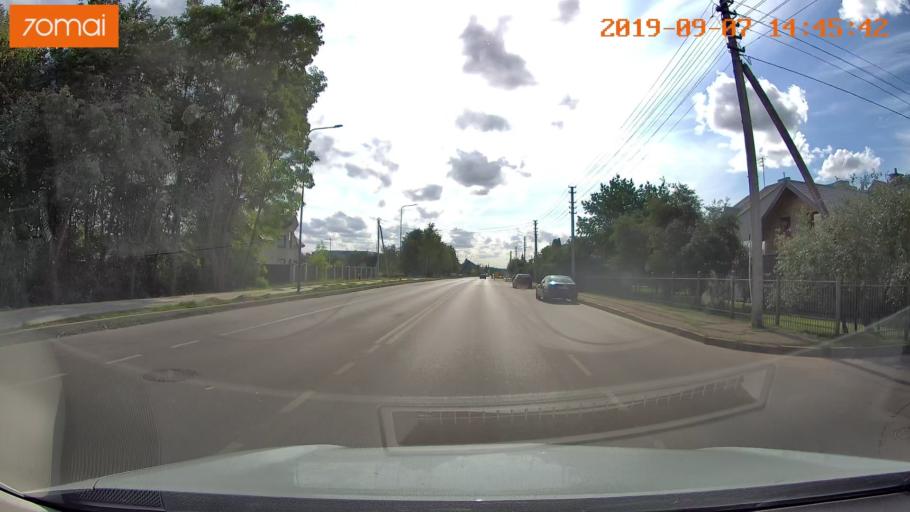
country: LT
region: Kauno apskritis
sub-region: Kaunas
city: Silainiai
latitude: 54.9312
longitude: 23.9089
